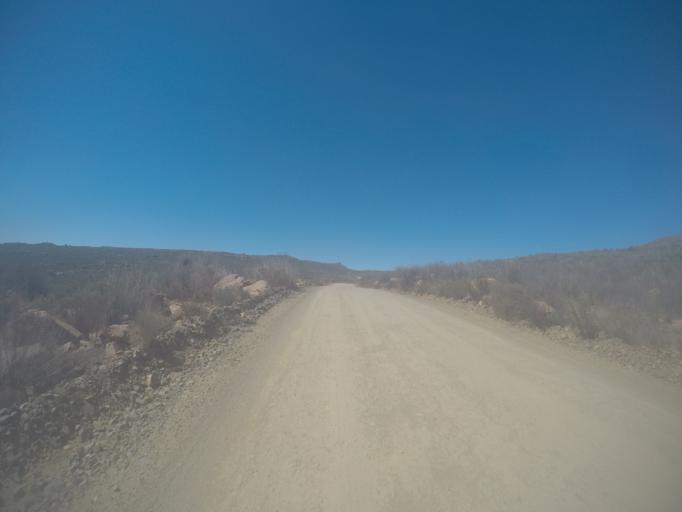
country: ZA
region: Western Cape
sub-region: West Coast District Municipality
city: Clanwilliam
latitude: -32.5042
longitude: 19.2817
